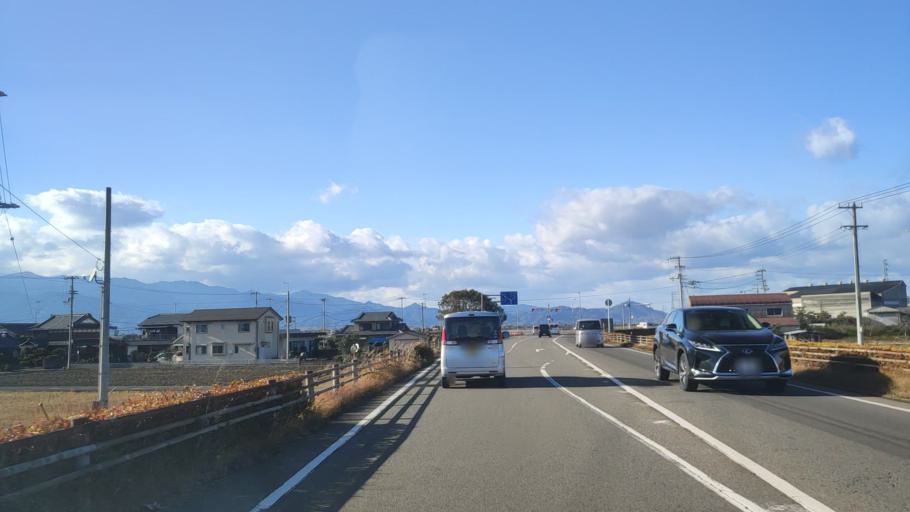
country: JP
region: Ehime
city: Saijo
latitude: 33.9182
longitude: 133.1261
